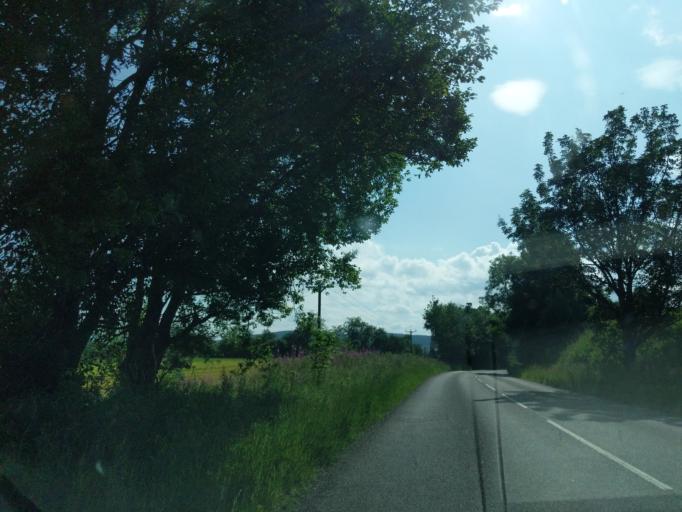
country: GB
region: Scotland
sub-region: Moray
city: Rothes
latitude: 57.5412
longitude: -3.1908
